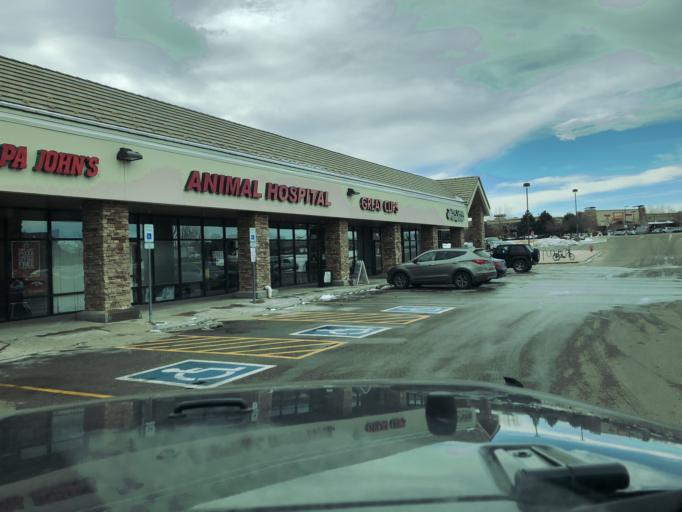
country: US
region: Colorado
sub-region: Boulder County
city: Longmont
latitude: 40.1870
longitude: -105.0728
